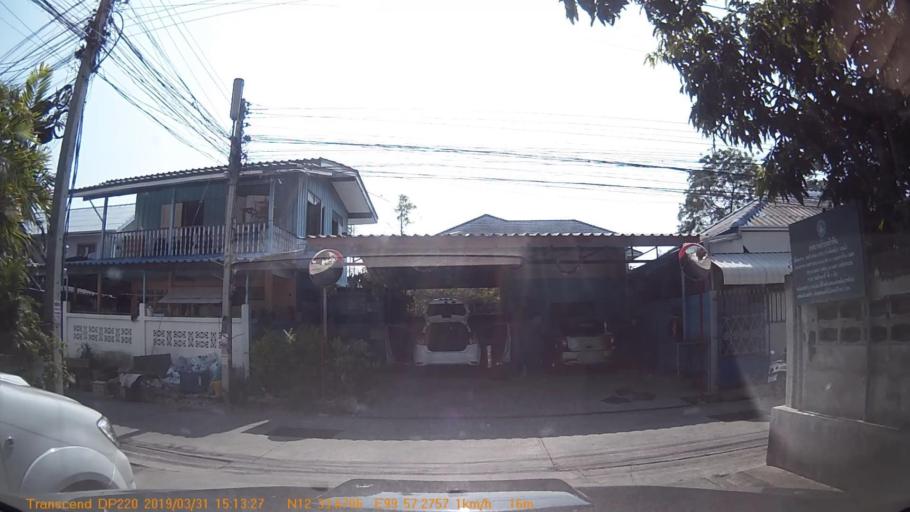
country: TH
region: Prachuap Khiri Khan
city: Hua Hin
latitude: 12.5612
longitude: 99.9546
